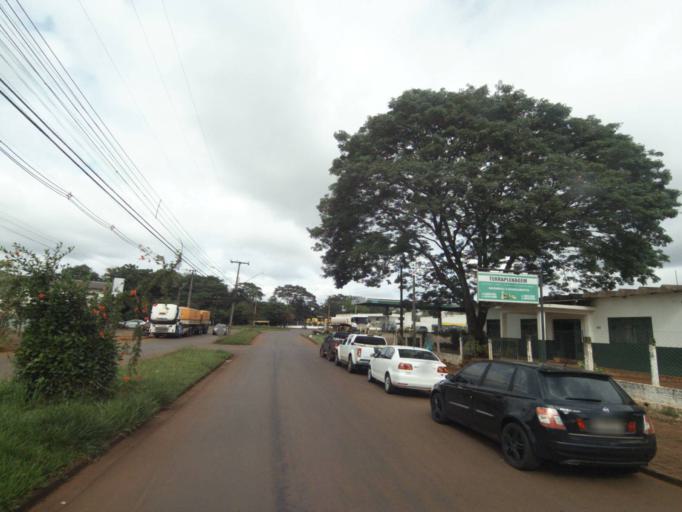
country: BR
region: Parana
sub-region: Campo Mourao
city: Campo Mourao
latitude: -24.0531
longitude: -52.3821
